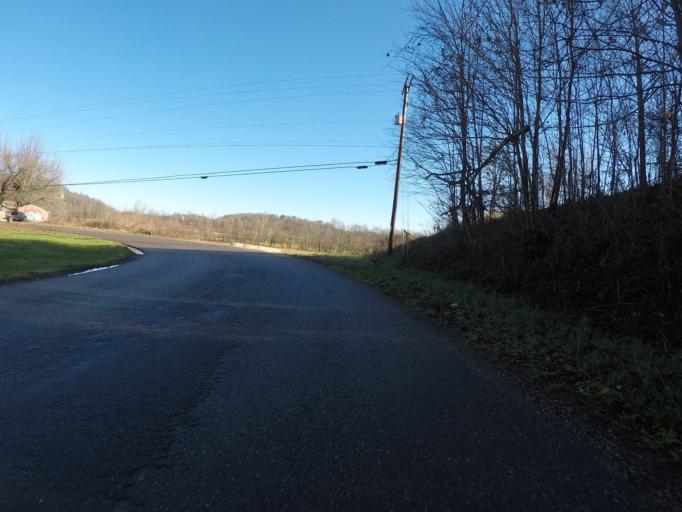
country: US
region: West Virginia
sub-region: Cabell County
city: Huntington
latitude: 38.4803
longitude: -82.4676
